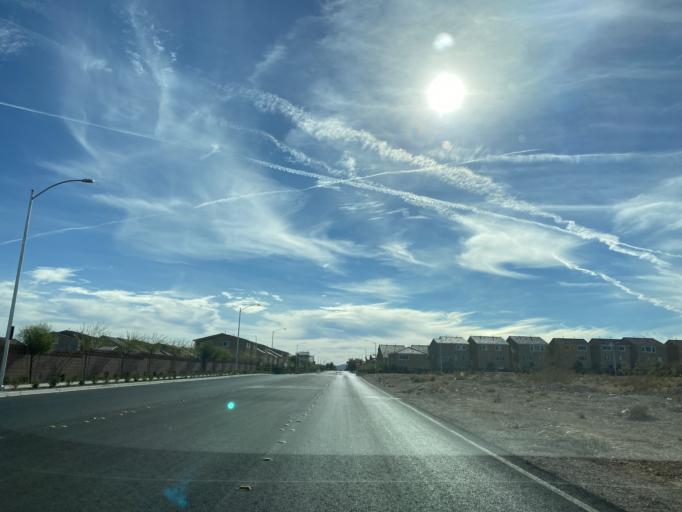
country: US
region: Nevada
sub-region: Clark County
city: Enterprise
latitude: 36.0610
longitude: -115.2338
